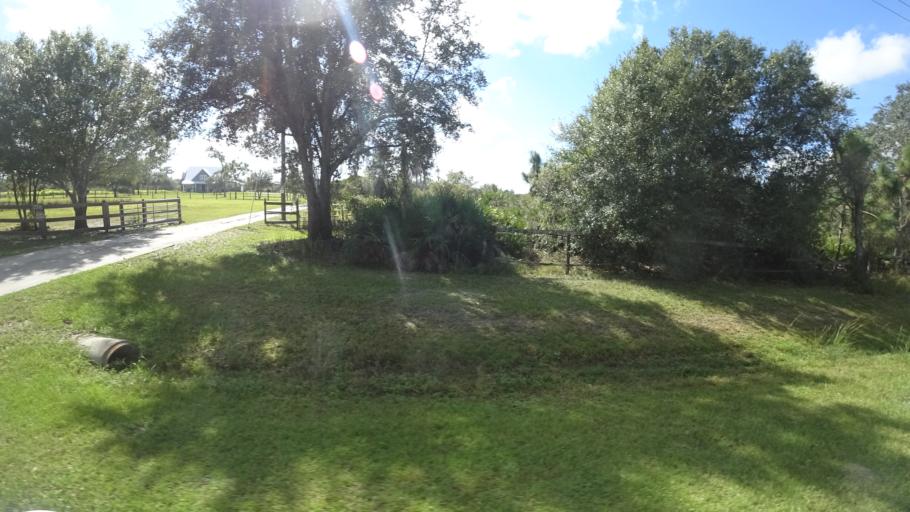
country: US
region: Florida
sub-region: Sarasota County
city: Lake Sarasota
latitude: 27.3682
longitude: -82.1430
